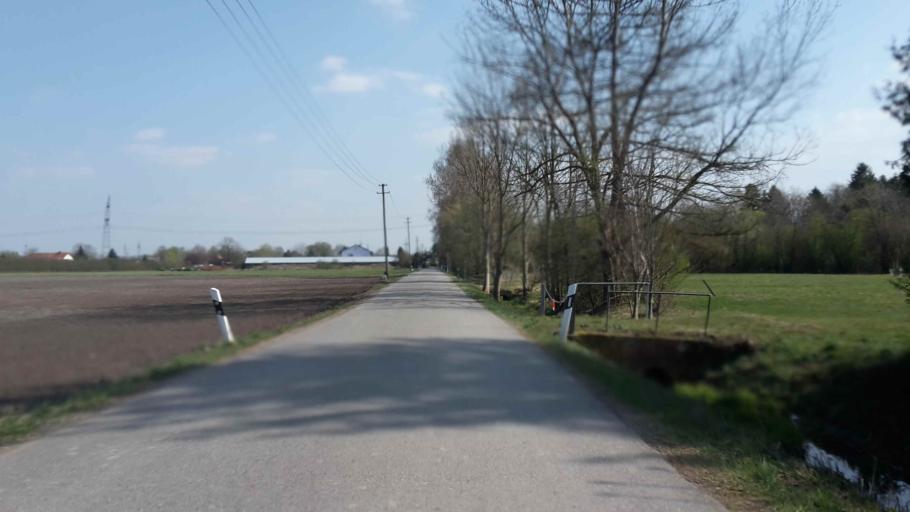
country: DE
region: Bavaria
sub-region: Upper Bavaria
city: Karlsfeld
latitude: 48.1914
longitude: 11.4221
